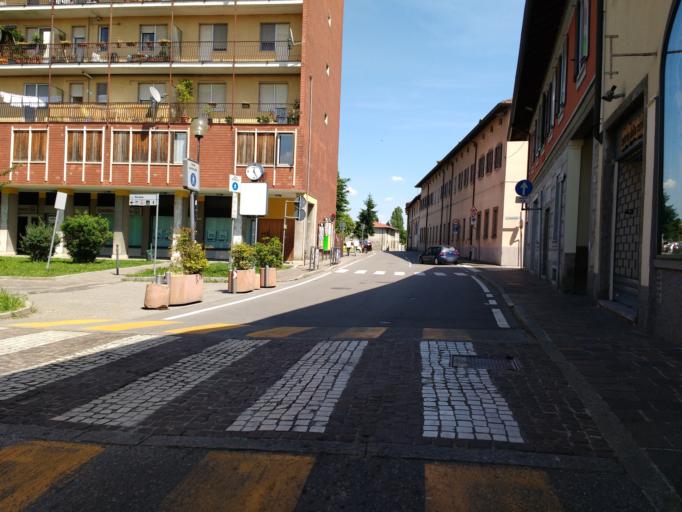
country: IT
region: Lombardy
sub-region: Citta metropolitana di Milano
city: Vignate
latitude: 45.4953
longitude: 9.3768
